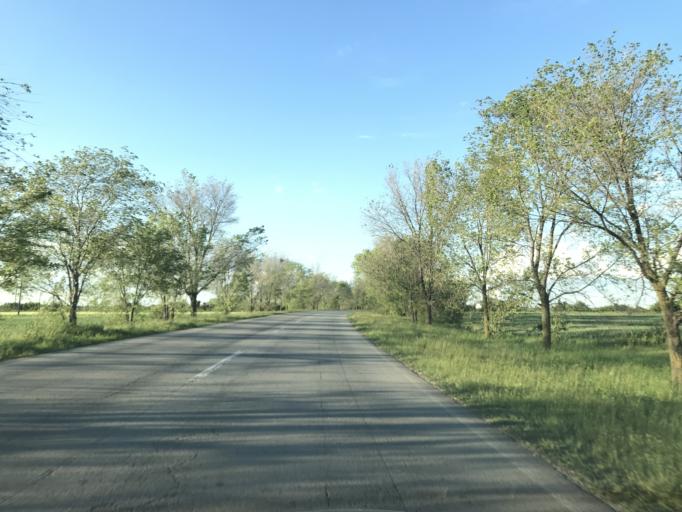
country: RS
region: Autonomna Pokrajina Vojvodina
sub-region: Srednjebanatski Okrug
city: Zrenjanin
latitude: 45.3915
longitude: 20.3535
